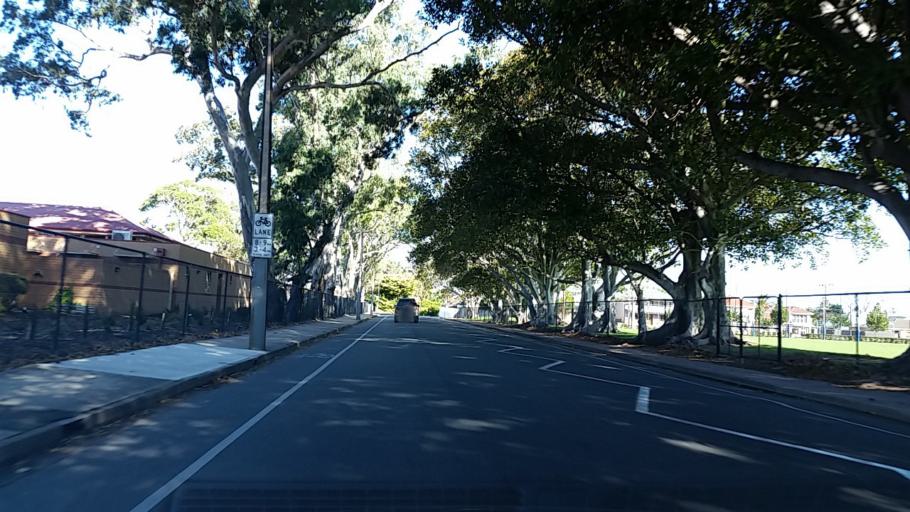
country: AU
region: South Australia
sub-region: Holdfast Bay
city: North Brighton
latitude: -34.9954
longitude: 138.5191
